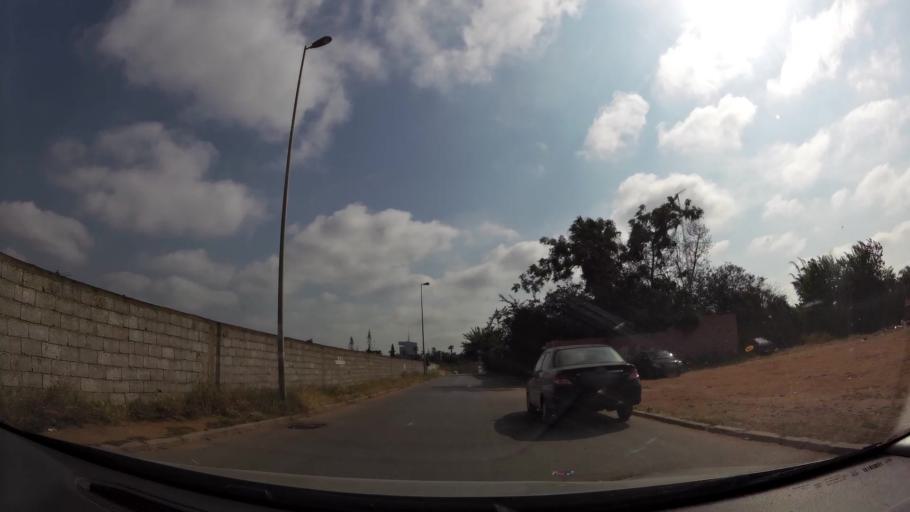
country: MA
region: Rabat-Sale-Zemmour-Zaer
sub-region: Rabat
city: Rabat
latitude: 33.9697
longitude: -6.8620
